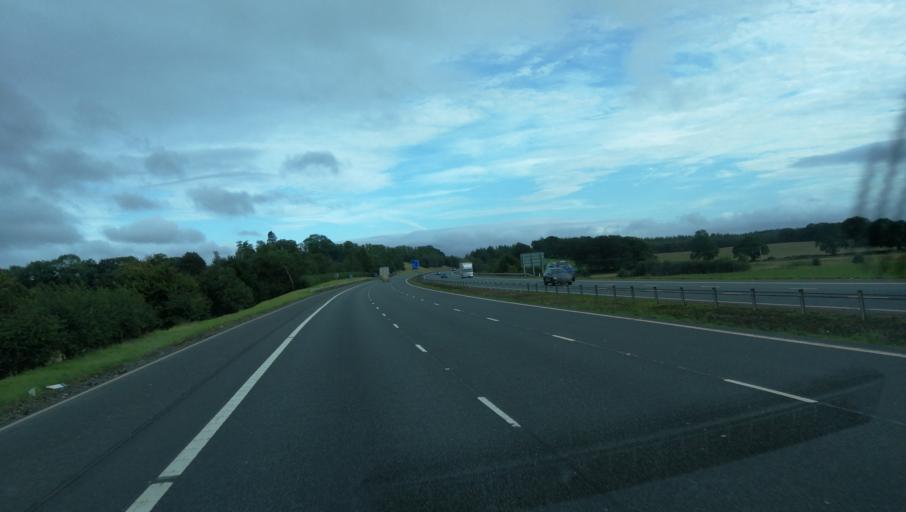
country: GB
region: Scotland
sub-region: Dumfries and Galloway
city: Lockerbie
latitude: 55.1430
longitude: -3.3749
